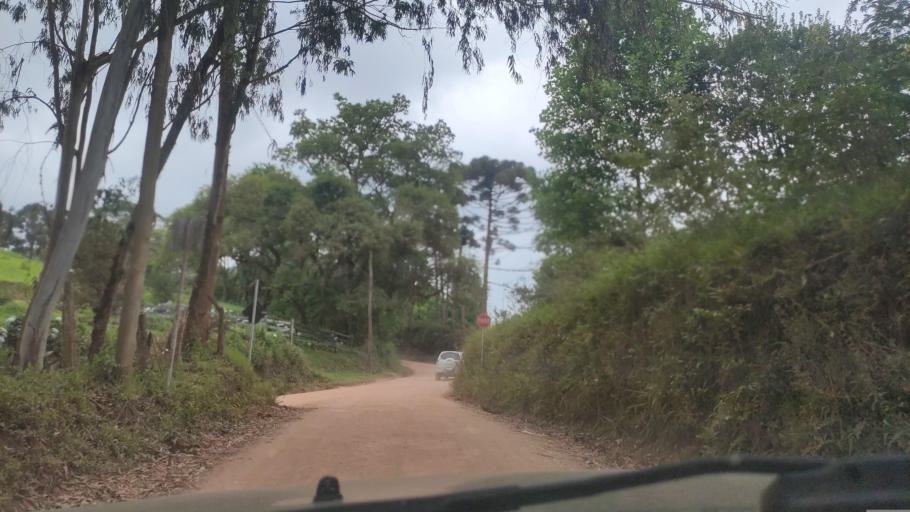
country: BR
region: Minas Gerais
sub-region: Paraisopolis
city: Paraisopolis
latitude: -22.6608
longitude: -45.8634
